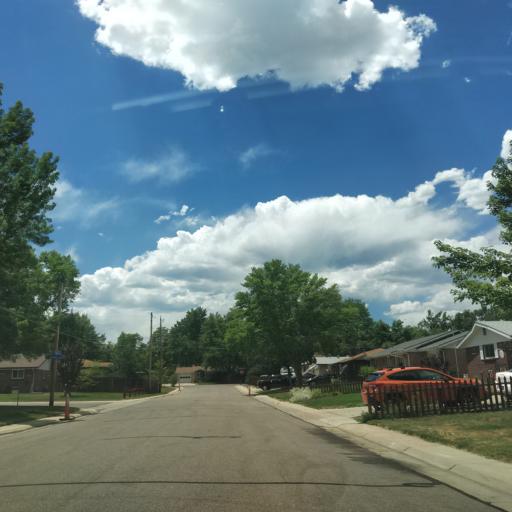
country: US
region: Colorado
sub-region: Jefferson County
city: Lakewood
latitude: 39.6887
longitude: -105.0876
